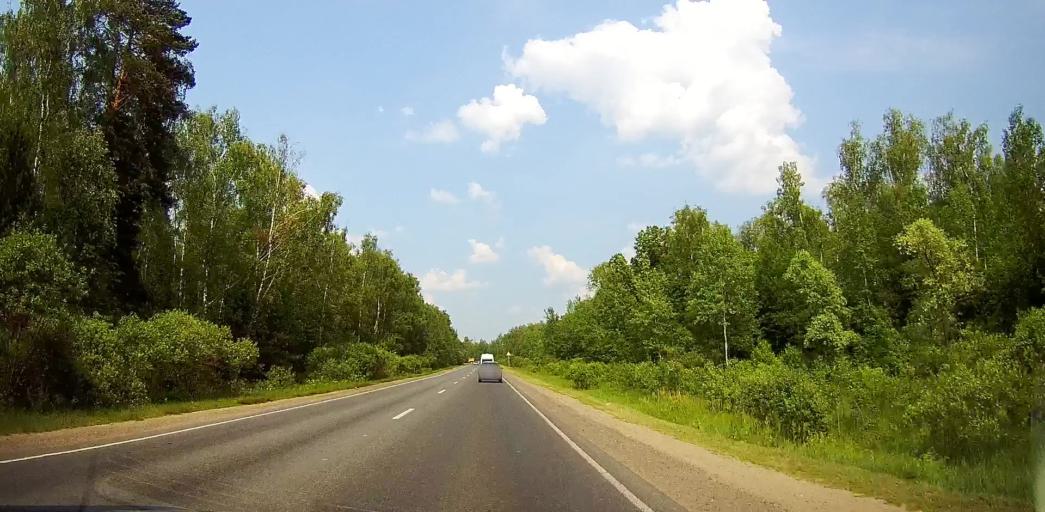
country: RU
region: Moskovskaya
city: Stupino
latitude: 54.9207
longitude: 38.1110
